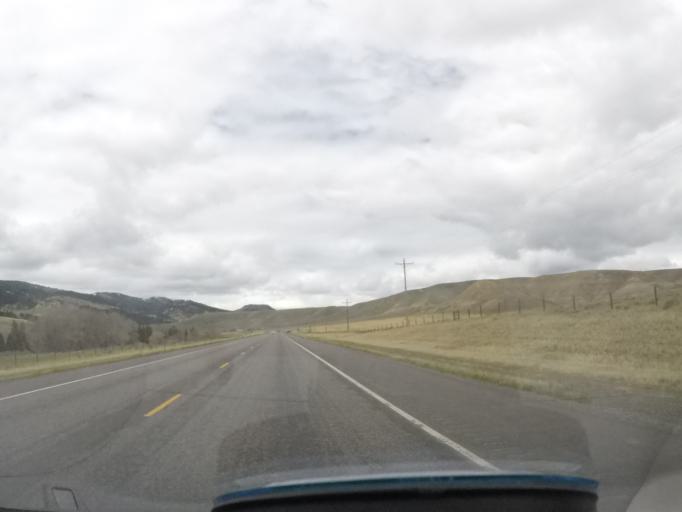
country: US
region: Wyoming
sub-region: Sublette County
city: Pinedale
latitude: 43.5757
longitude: -109.7340
